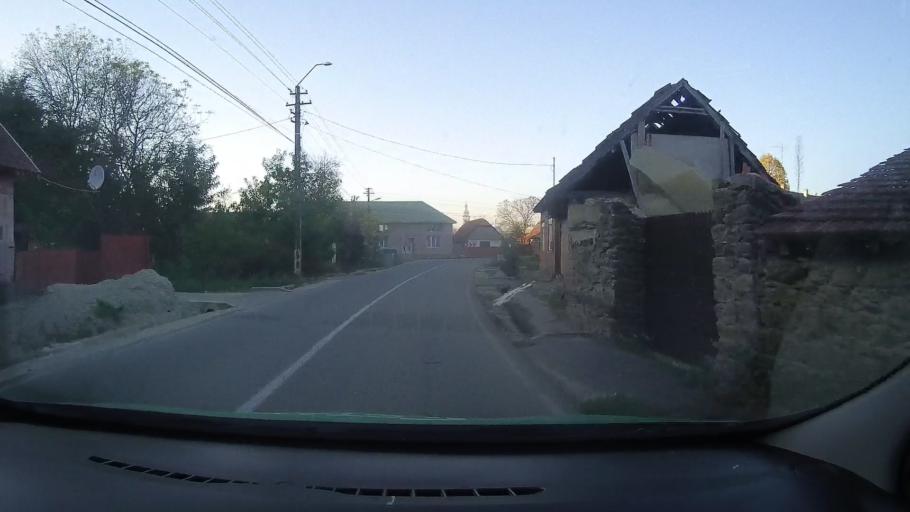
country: RO
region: Timis
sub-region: Comuna Traian Vuia
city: Traian Vuia
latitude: 45.7645
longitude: 22.0954
